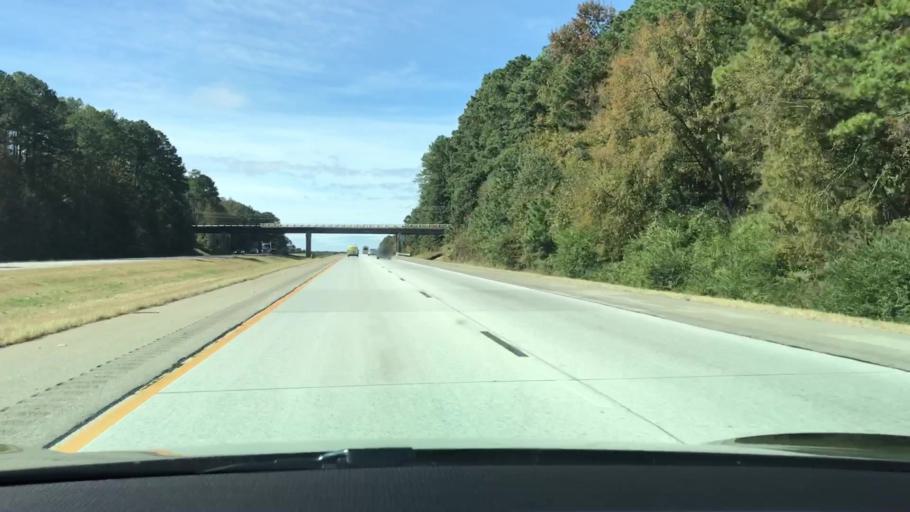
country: US
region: Georgia
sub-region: Greene County
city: Greensboro
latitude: 33.5393
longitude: -83.2337
